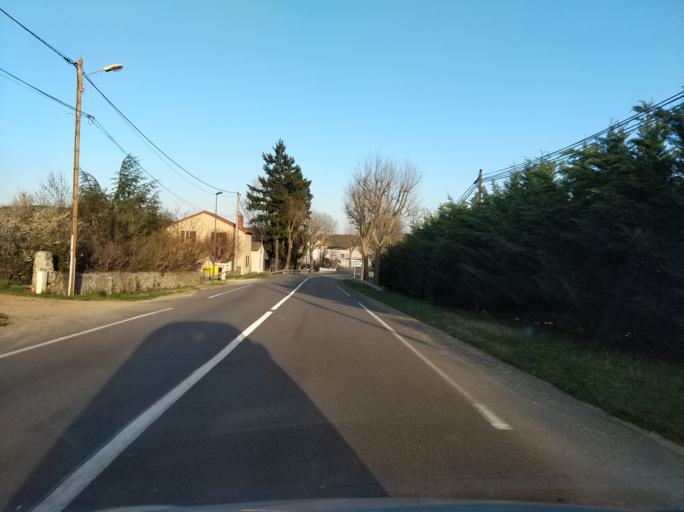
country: FR
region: Rhone-Alpes
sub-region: Departement de l'Ardeche
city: Boulieu-les-Annonay
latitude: 45.2696
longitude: 4.6780
